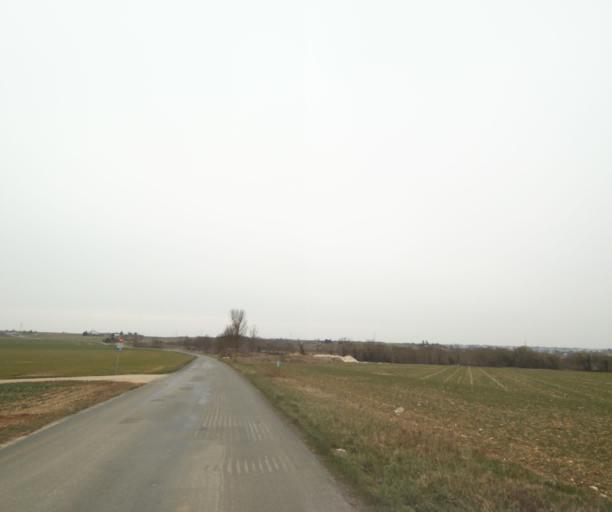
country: FR
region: Poitou-Charentes
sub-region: Departement des Deux-Sevres
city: Bessines
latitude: 46.3401
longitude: -0.5131
